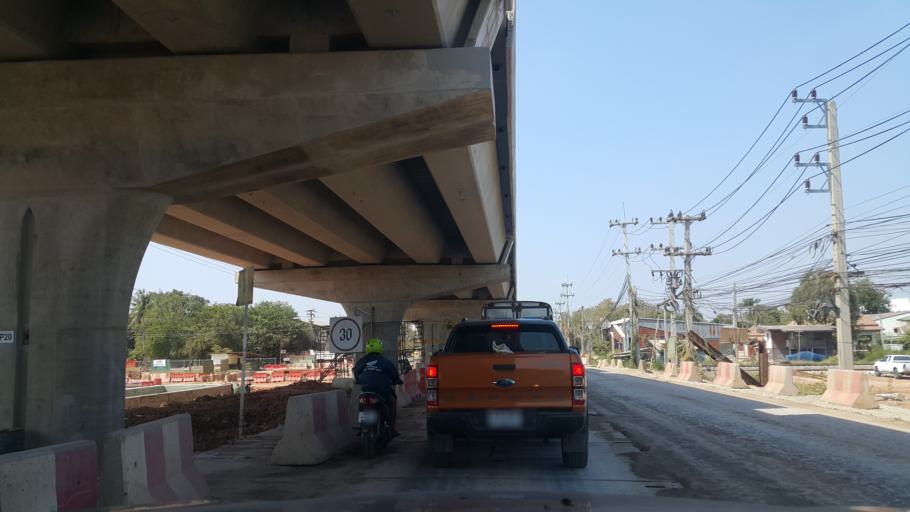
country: TH
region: Nakhon Ratchasima
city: Bua Yai
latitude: 15.5911
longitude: 102.4327
